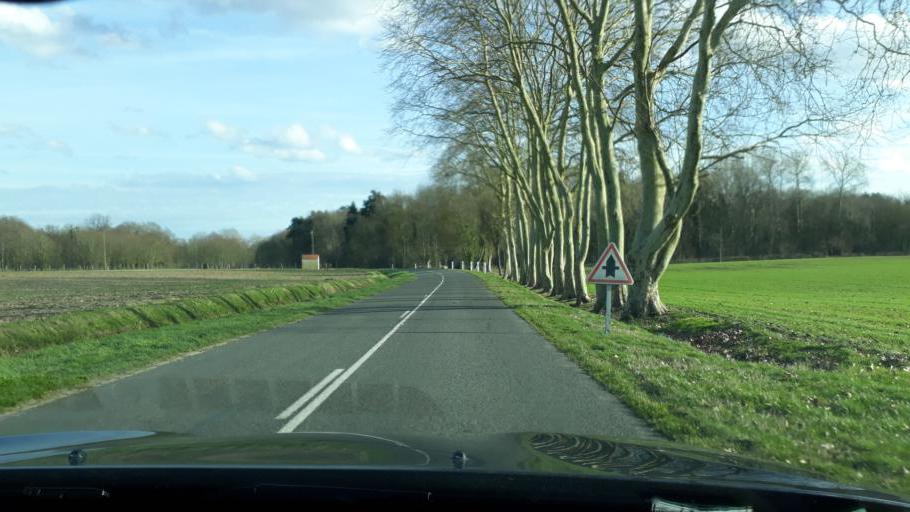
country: FR
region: Centre
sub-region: Departement du Loiret
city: Chilleurs-aux-Bois
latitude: 48.0636
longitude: 2.1525
